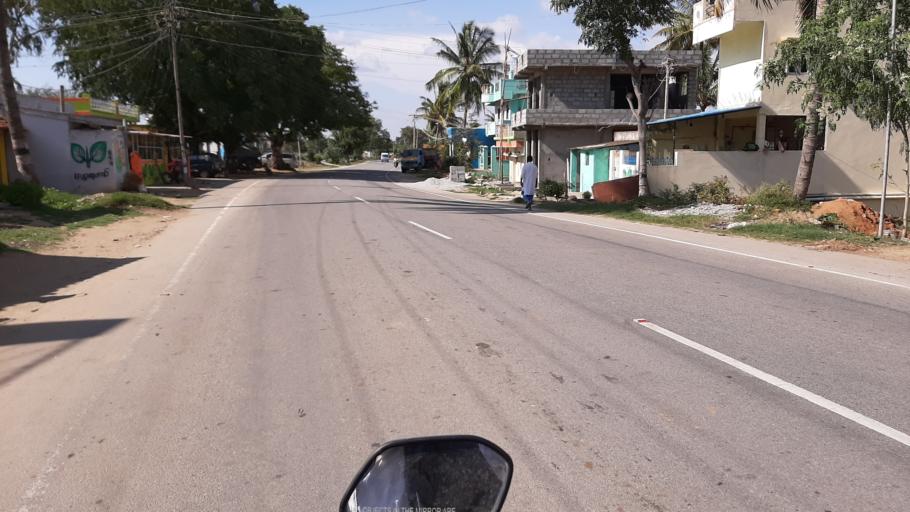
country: IN
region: Tamil Nadu
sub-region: Krishnagiri
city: Denkanikota
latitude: 12.5600
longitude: 77.7842
